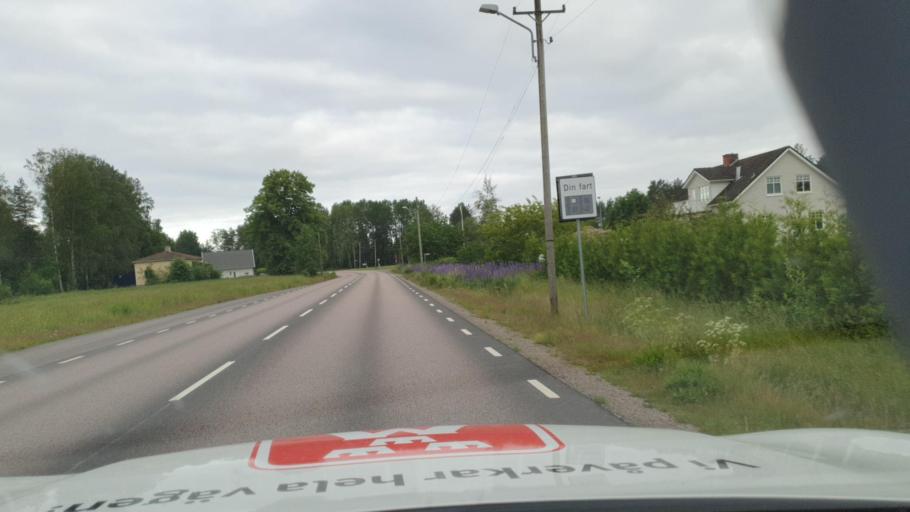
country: SE
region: Vaermland
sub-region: Forshaga Kommun
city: Forshaga
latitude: 59.4536
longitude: 13.4228
